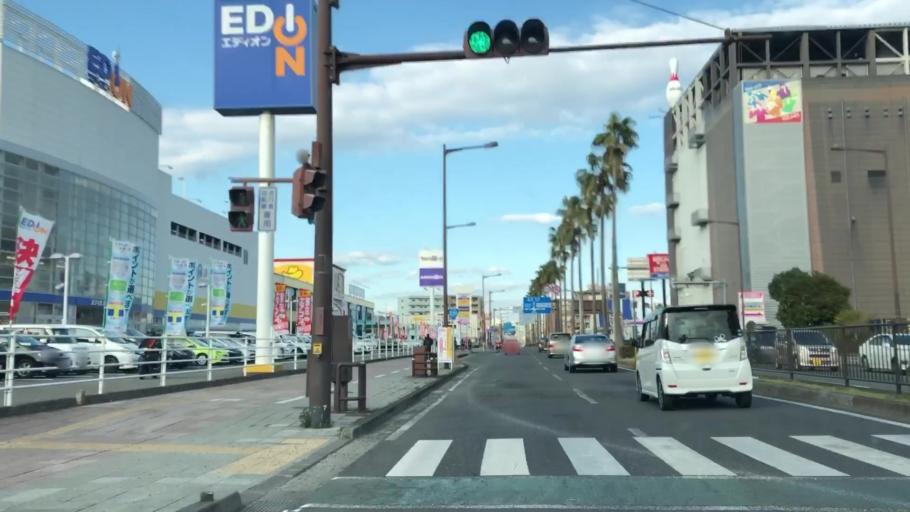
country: JP
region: Miyazaki
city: Miyazaki-shi
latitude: 31.8946
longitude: 131.4167
